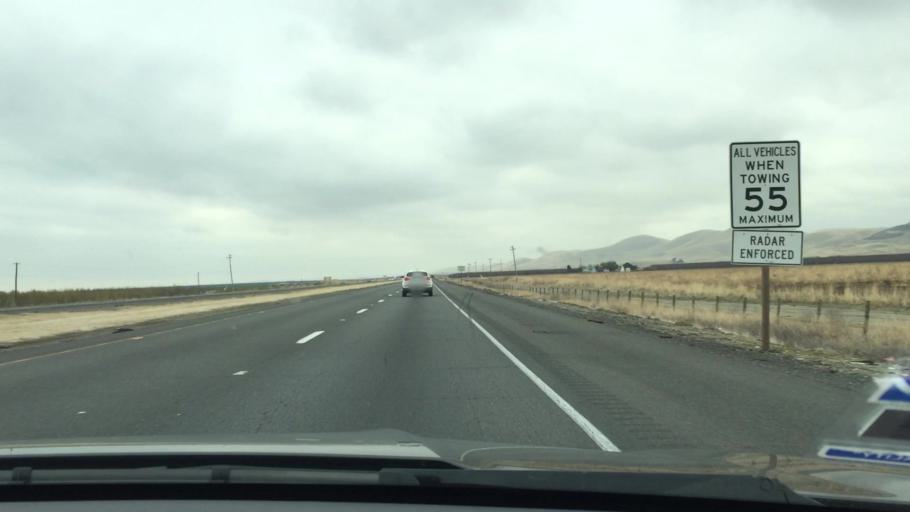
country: US
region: California
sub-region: Merced County
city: Gustine
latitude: 37.2388
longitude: -121.0872
